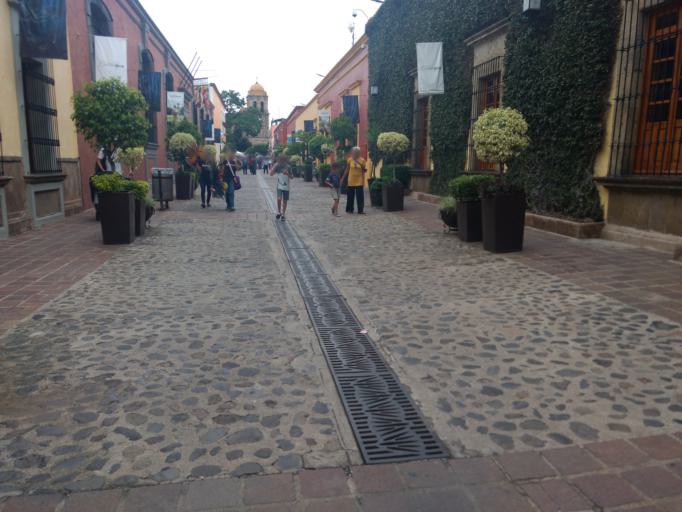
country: MX
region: Jalisco
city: Tequila
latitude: 20.8855
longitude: -103.8405
